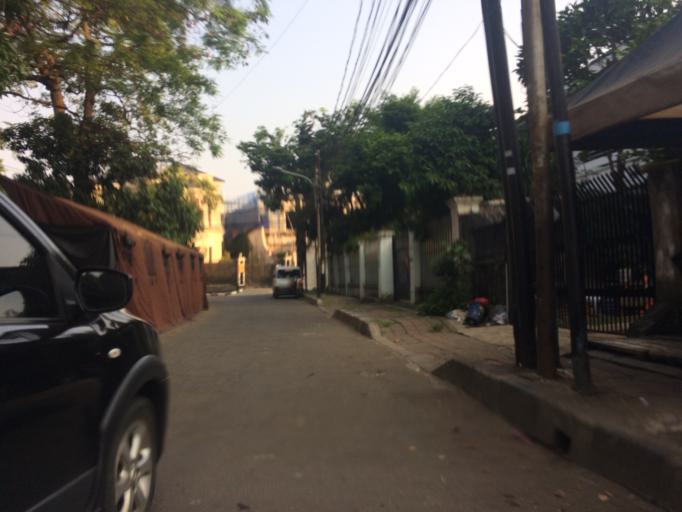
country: ID
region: Jakarta Raya
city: Jakarta
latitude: -6.2018
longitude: 106.8427
